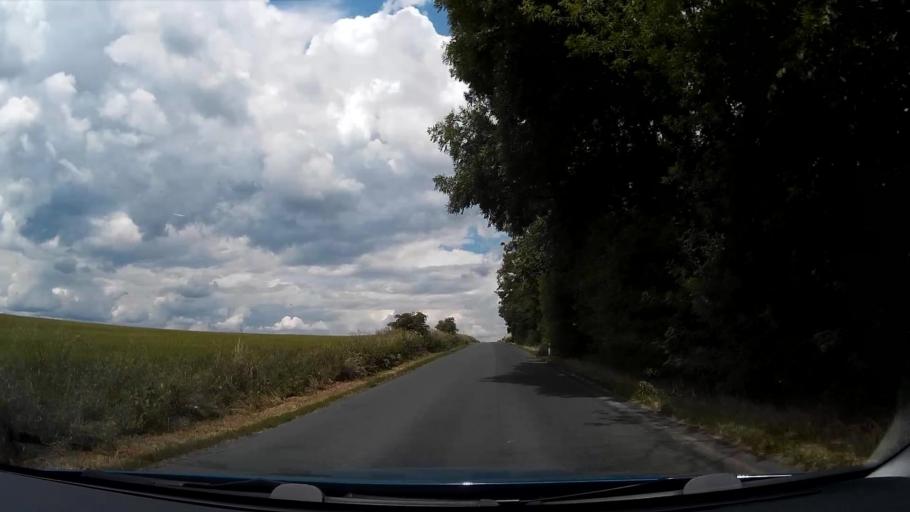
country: CZ
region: South Moravian
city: Orechov
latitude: 49.0993
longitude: 16.5256
